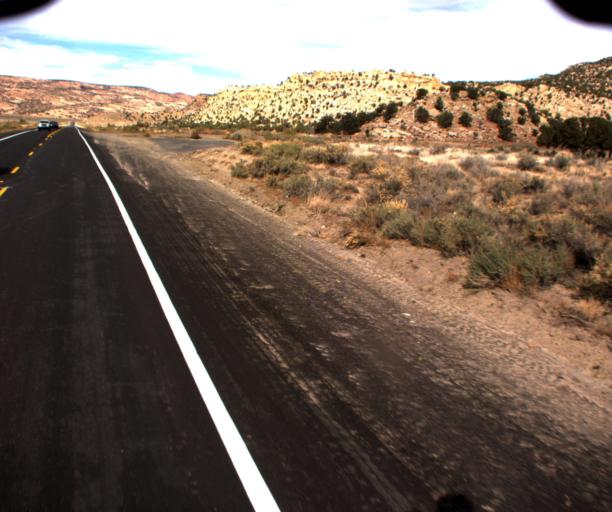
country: US
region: Arizona
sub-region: Navajo County
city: Kayenta
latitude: 36.5936
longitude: -110.4722
